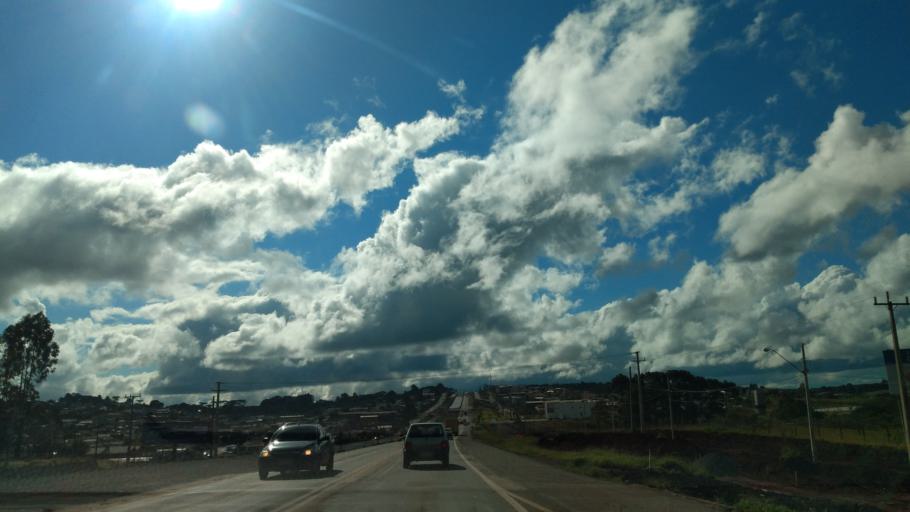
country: BR
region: Parana
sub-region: Guarapuava
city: Guarapuava
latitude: -25.3561
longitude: -51.4835
